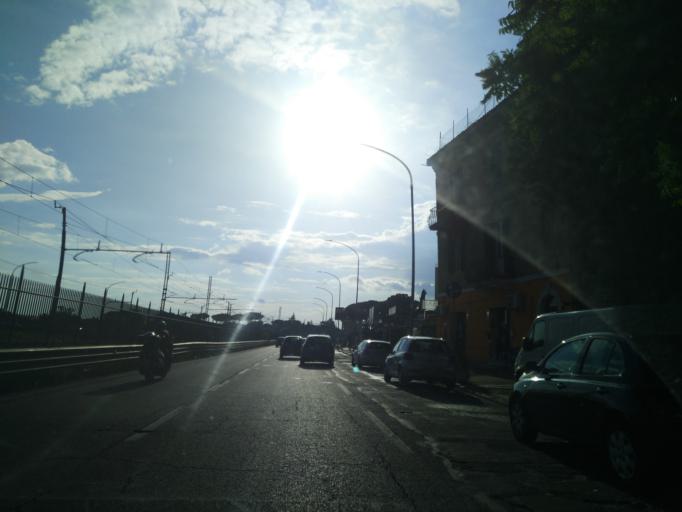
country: IT
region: Latium
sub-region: Citta metropolitana di Roma Capitale
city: Rome
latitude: 41.8753
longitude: 12.5599
